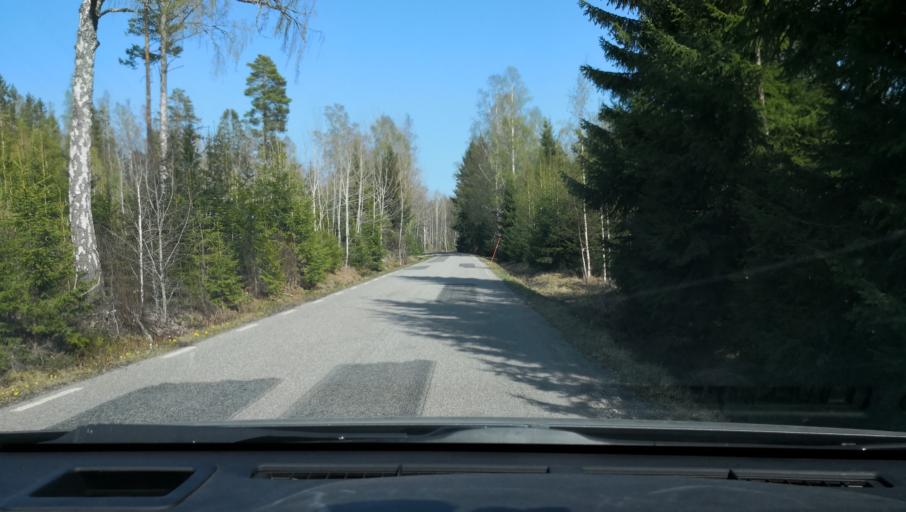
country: SE
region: Uppsala
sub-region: Heby Kommun
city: Heby
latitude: 60.0439
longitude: 16.8426
